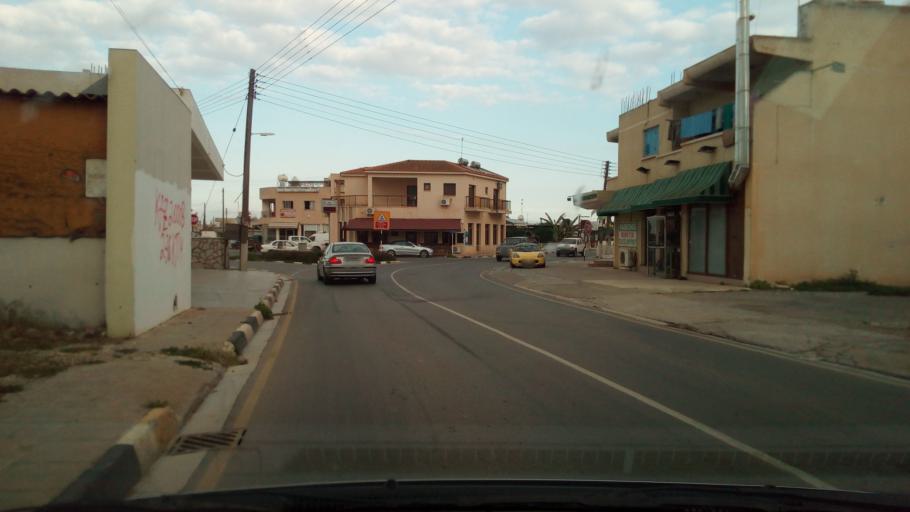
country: CY
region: Ammochostos
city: Liopetri
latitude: 34.9774
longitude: 33.8507
